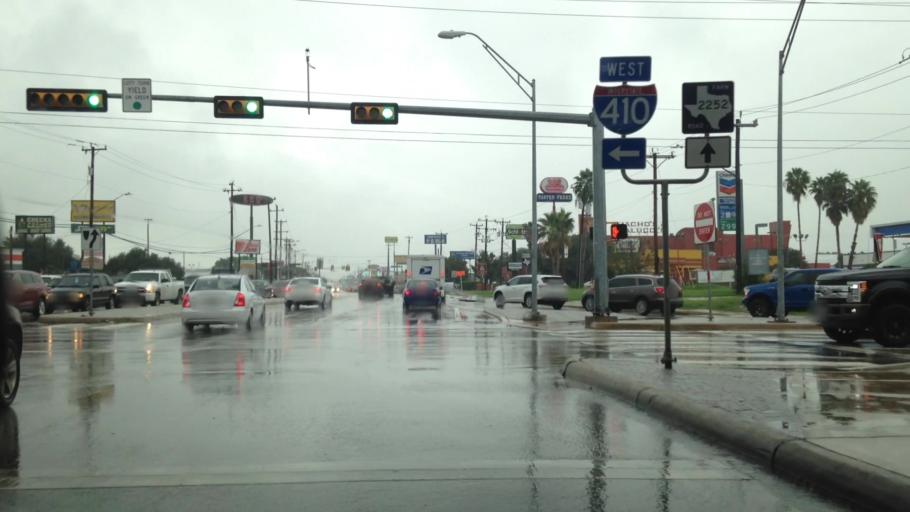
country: US
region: Texas
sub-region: Bexar County
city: Windcrest
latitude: 29.5162
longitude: -98.4110
